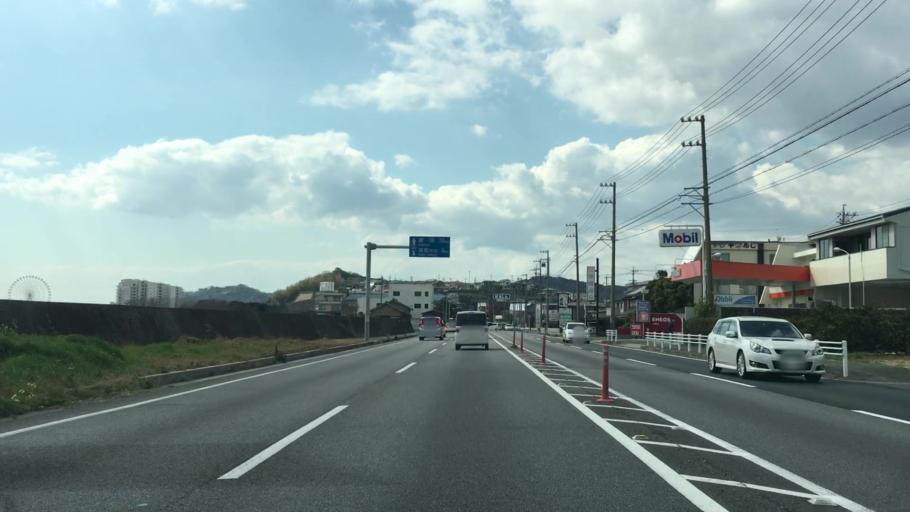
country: JP
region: Aichi
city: Gamagori
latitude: 34.8130
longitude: 137.2898
